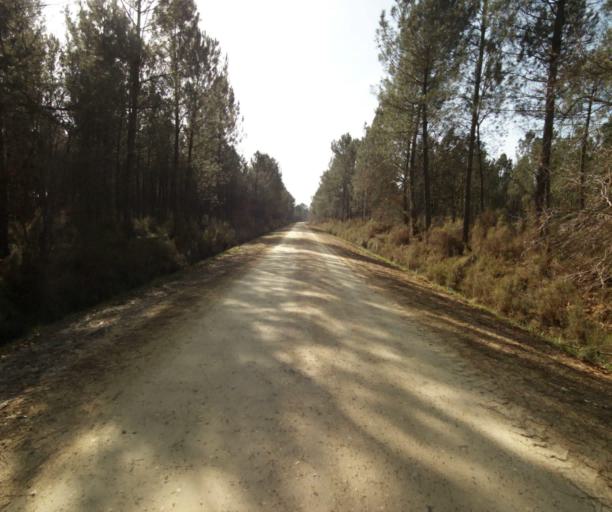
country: FR
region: Aquitaine
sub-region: Departement de la Gironde
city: Grignols
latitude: 44.2208
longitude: -0.1418
